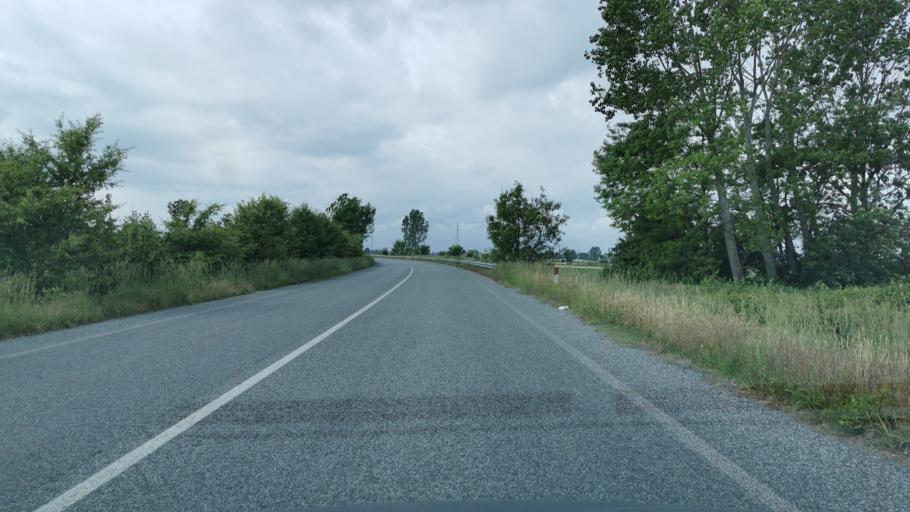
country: IT
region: Piedmont
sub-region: Provincia di Cuneo
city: Racconigi
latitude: 44.7881
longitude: 7.7001
